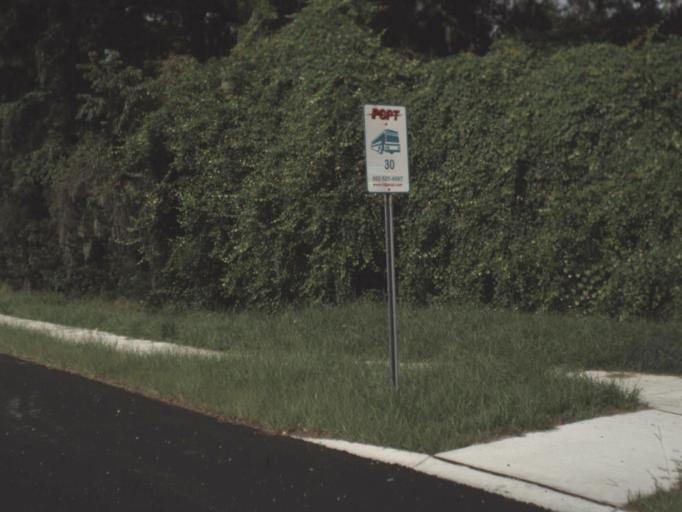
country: US
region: Florida
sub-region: Pasco County
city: Lacoochee
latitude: 28.4406
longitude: -82.1902
